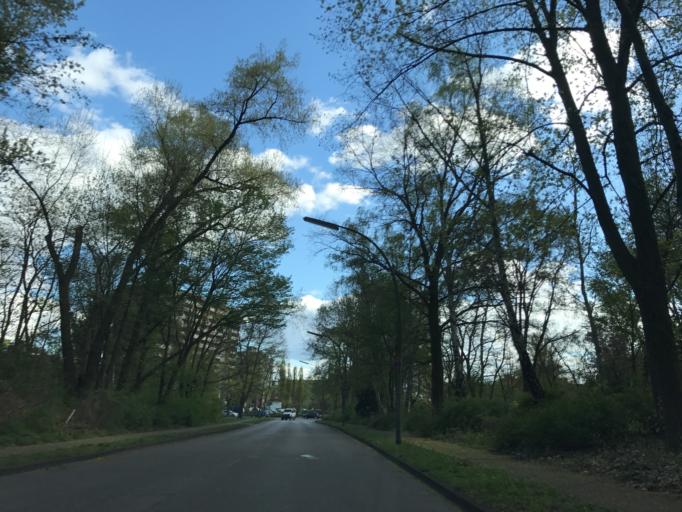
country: DE
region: Berlin
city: Tegel
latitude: 52.5788
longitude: 13.2752
